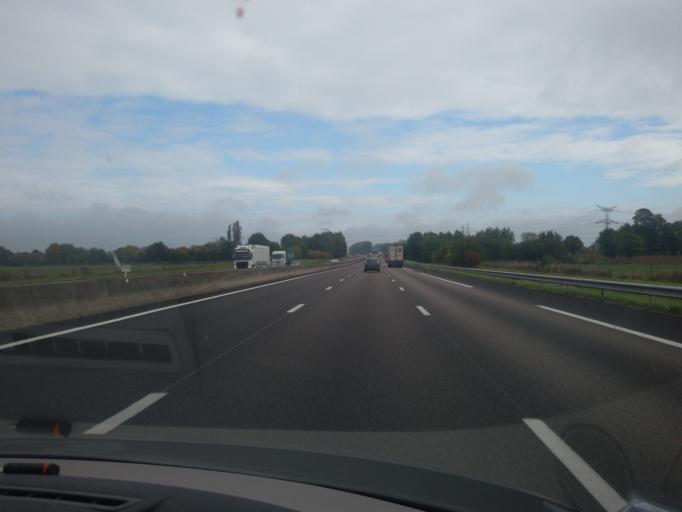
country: FR
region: Haute-Normandie
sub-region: Departement de l'Eure
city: Hauville
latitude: 49.3701
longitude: 0.7330
